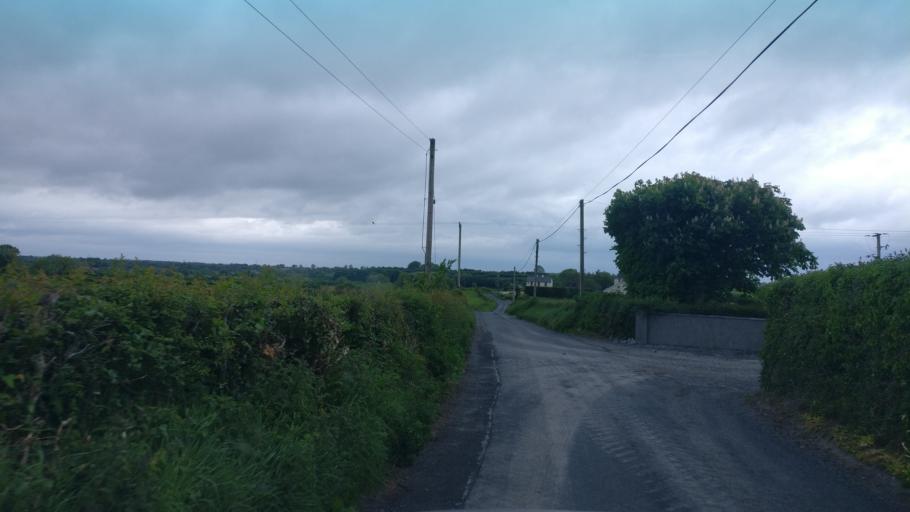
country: IE
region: Connaught
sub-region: County Galway
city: Portumna
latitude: 53.1449
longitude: -8.2874
